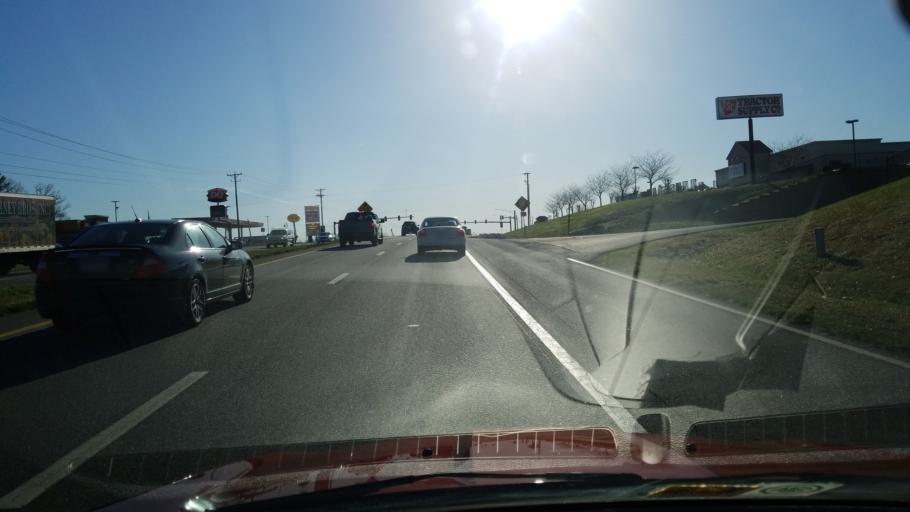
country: US
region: Virginia
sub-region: Franklin County
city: Rocky Mount
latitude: 37.0721
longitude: -79.8998
